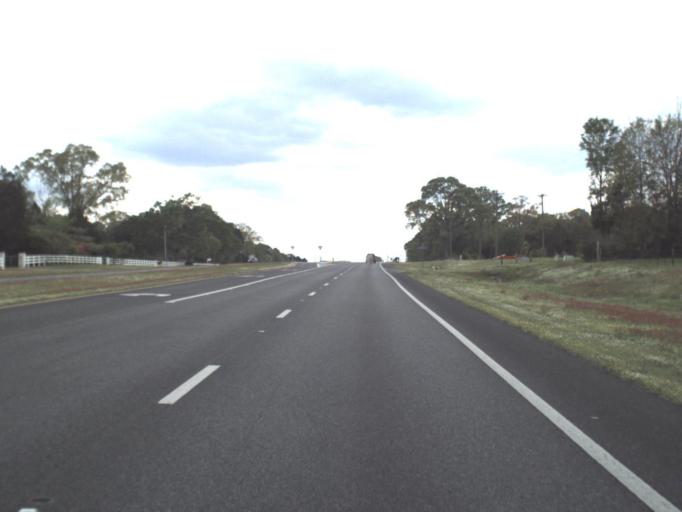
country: US
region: Florida
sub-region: Okaloosa County
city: Crestview
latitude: 30.8008
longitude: -86.5557
